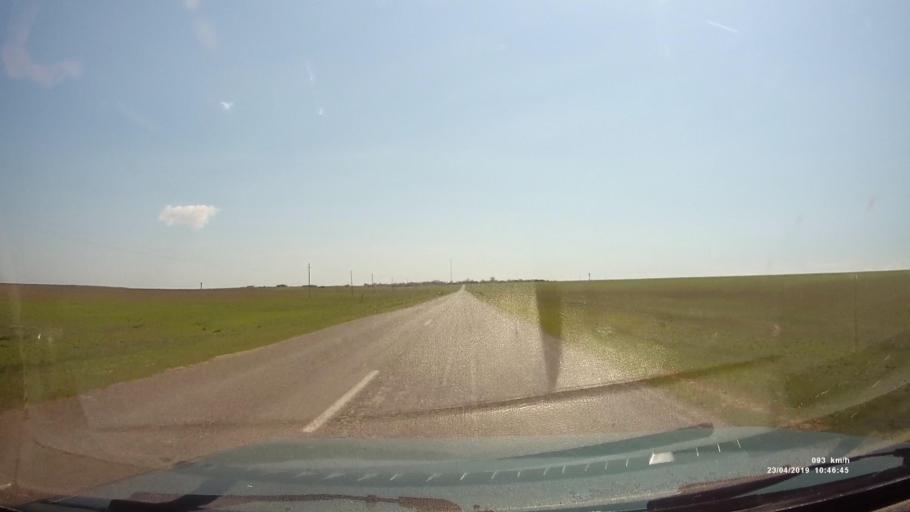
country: RU
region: Kalmykiya
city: Yashalta
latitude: 46.4404
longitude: 42.6963
